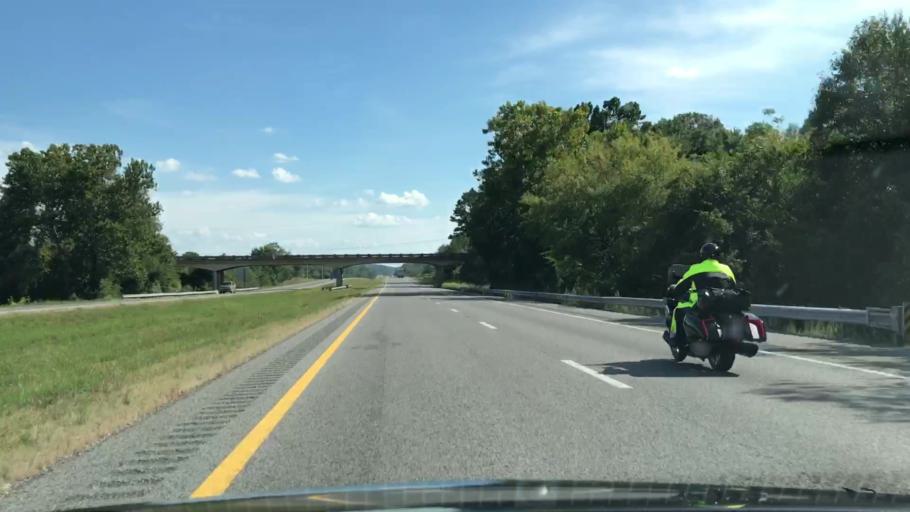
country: US
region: Alabama
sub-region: Limestone County
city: Ardmore
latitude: 35.0636
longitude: -86.8819
